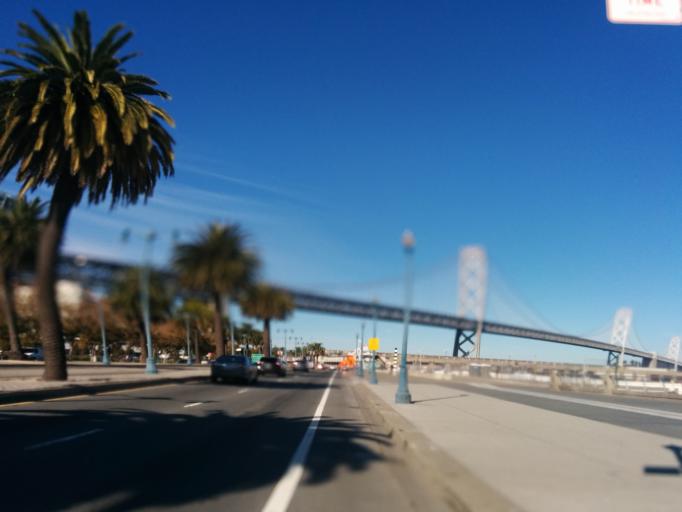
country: US
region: California
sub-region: San Francisco County
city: San Francisco
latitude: 37.7850
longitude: -122.3878
